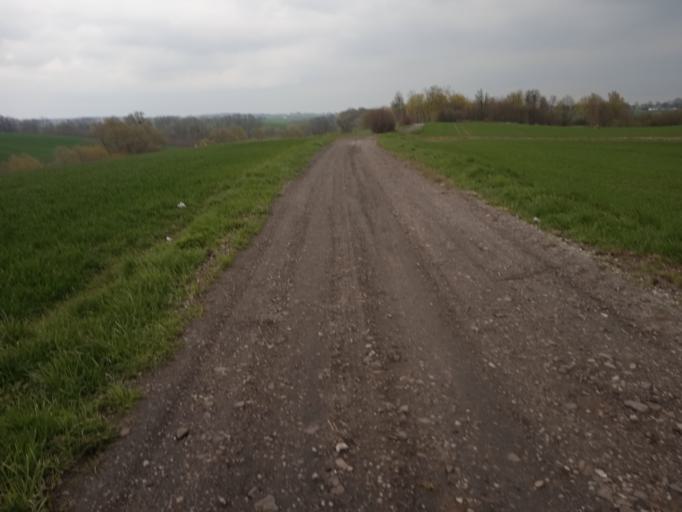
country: PL
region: Kujawsko-Pomorskie
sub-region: Powiat grudziadzki
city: Lasin
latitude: 53.5719
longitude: 19.0576
